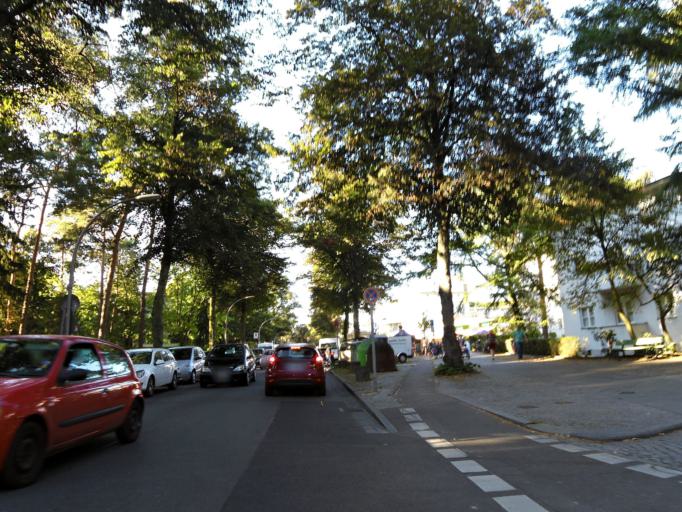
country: DE
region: Berlin
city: Zehlendorf Bezirk
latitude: 52.4487
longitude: 13.2518
